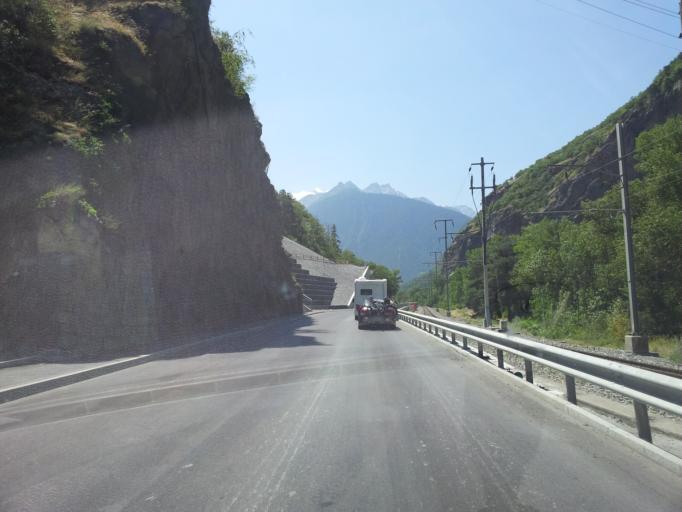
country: CH
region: Valais
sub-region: Visp District
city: Visp
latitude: 46.2777
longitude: 7.8829
